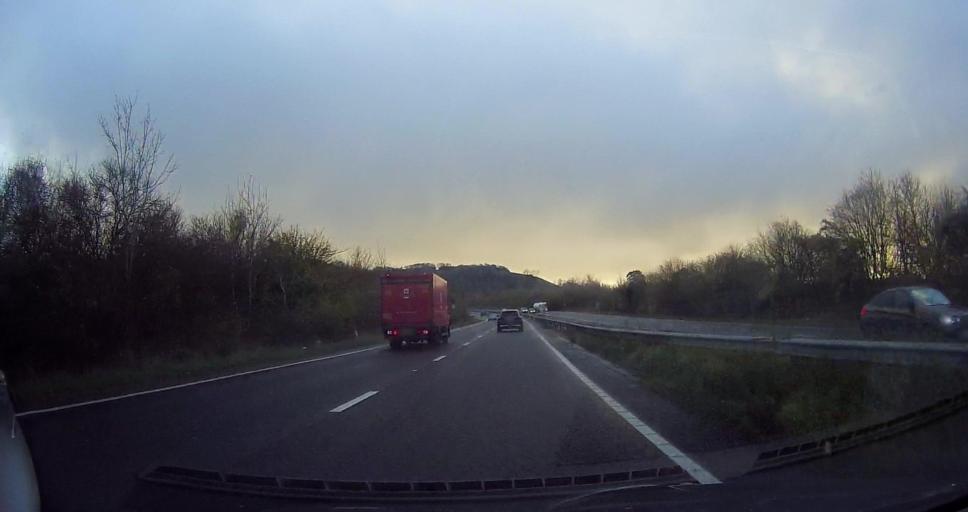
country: GB
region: England
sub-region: West Sussex
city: Hurstpierpoint
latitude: 50.9141
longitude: -0.1918
